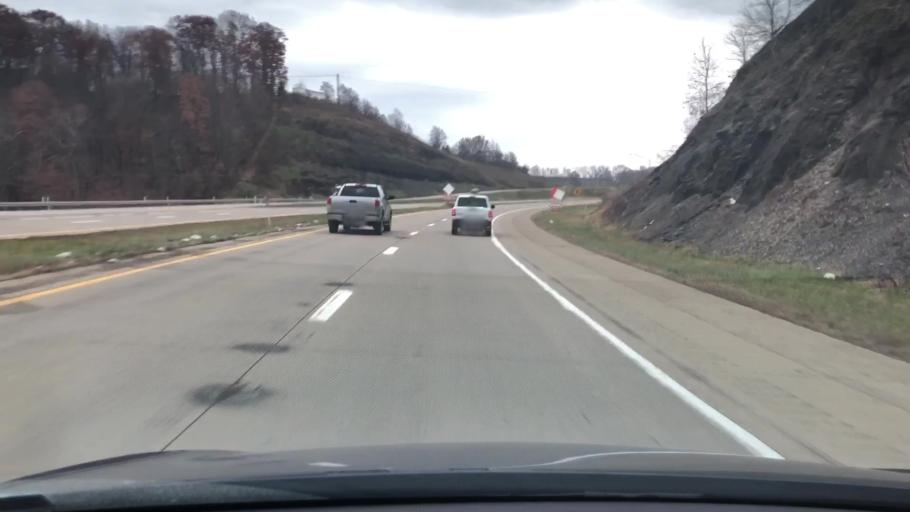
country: US
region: Pennsylvania
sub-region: Armstrong County
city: Kittanning
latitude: 40.8084
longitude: -79.4881
